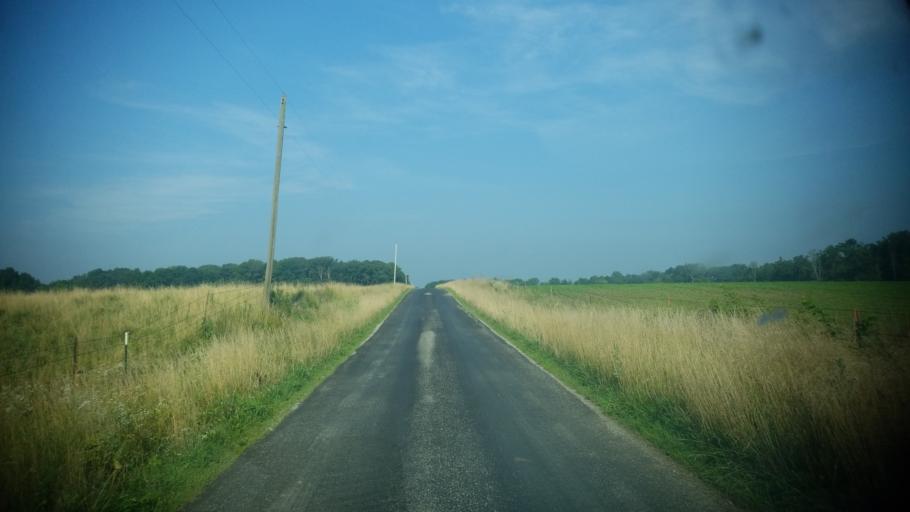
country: US
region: Illinois
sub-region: Clay County
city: Flora
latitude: 38.6026
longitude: -88.3935
